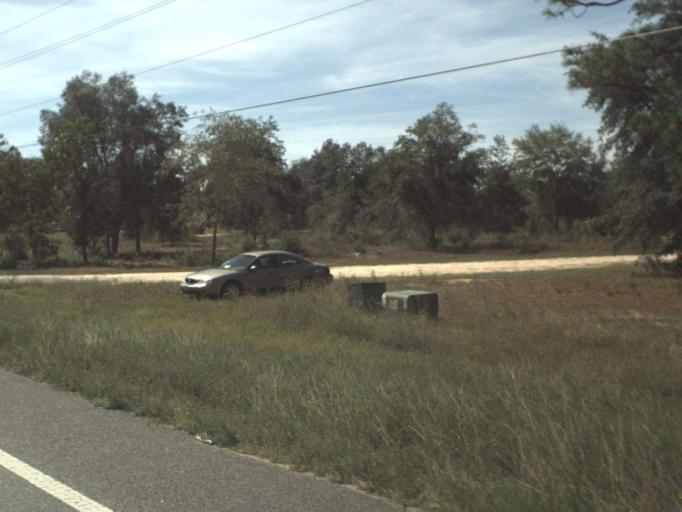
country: US
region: Florida
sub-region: Bay County
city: Youngstown
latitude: 30.5295
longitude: -85.6450
